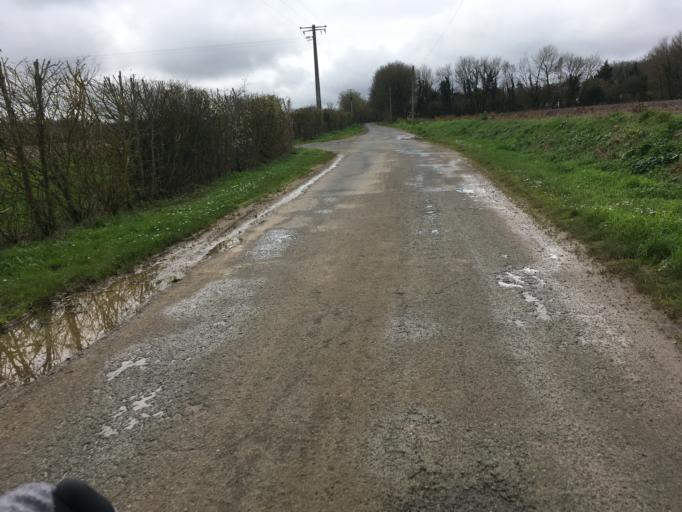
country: FR
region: Poitou-Charentes
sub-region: Departement de la Charente-Maritime
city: Saint-Germain-de-Marencennes
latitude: 46.1135
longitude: -0.7998
